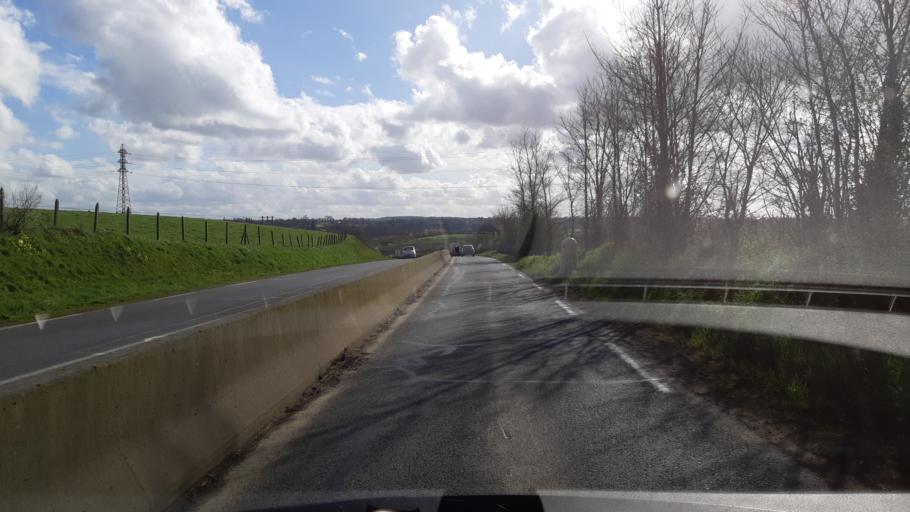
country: FR
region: Lower Normandy
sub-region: Departement de la Manche
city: Agneaux
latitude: 49.0979
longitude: -1.1205
